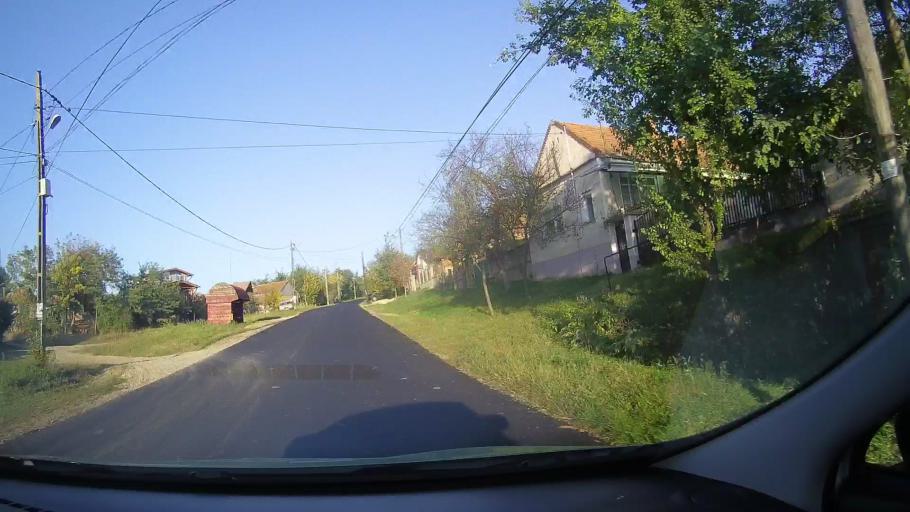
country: RO
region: Bihor
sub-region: Comuna Cetariu
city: Cetariu
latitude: 47.1347
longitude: 21.9893
